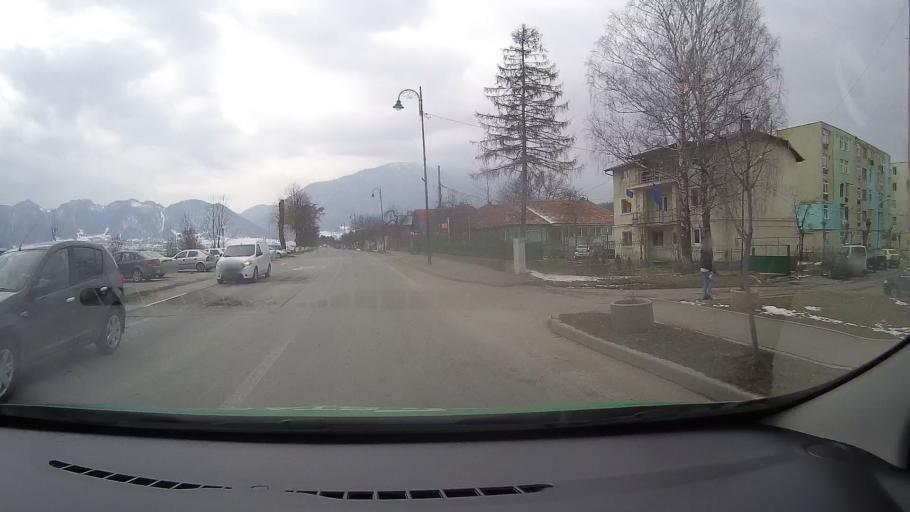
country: RO
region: Brasov
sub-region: Comuna Zarnesti
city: Zarnesti
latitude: 45.5687
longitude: 25.3488
